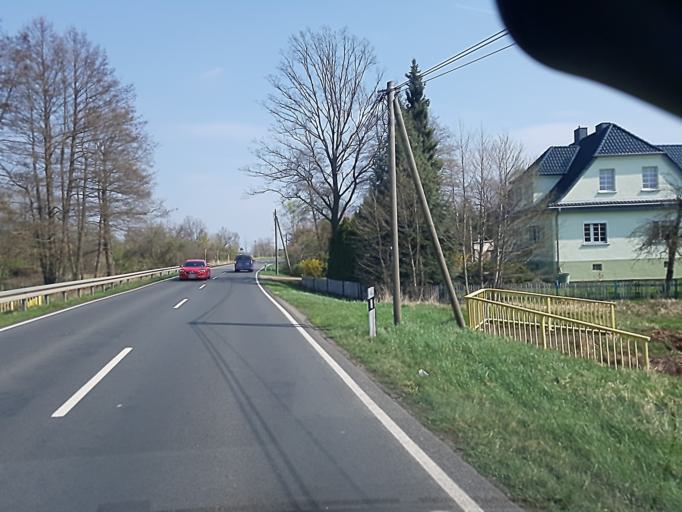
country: DE
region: Saxony-Anhalt
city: Grafenhainichen
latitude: 51.7295
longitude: 12.4679
